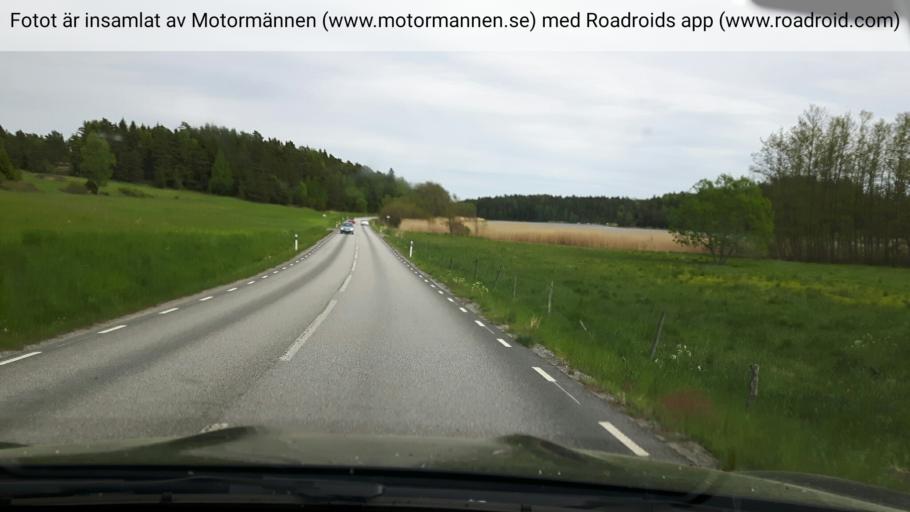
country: SE
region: Stockholm
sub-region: Norrtalje Kommun
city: Norrtalje
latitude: 59.6800
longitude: 18.7105
